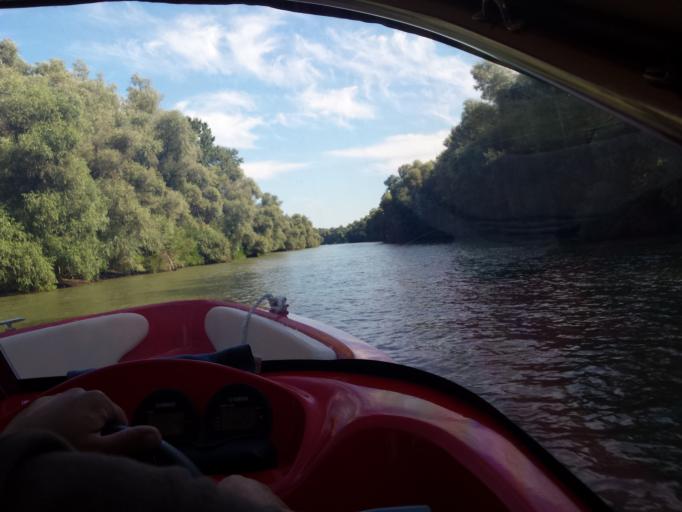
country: RO
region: Tulcea
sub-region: Comuna Pardina
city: Pardina
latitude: 45.2462
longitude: 28.9226
